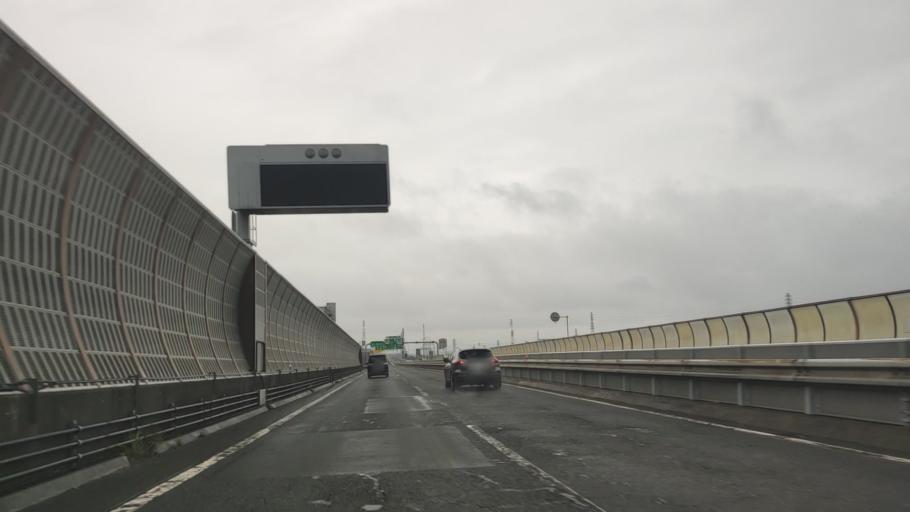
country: JP
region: Kanagawa
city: Chigasaki
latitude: 35.3502
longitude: 139.4050
